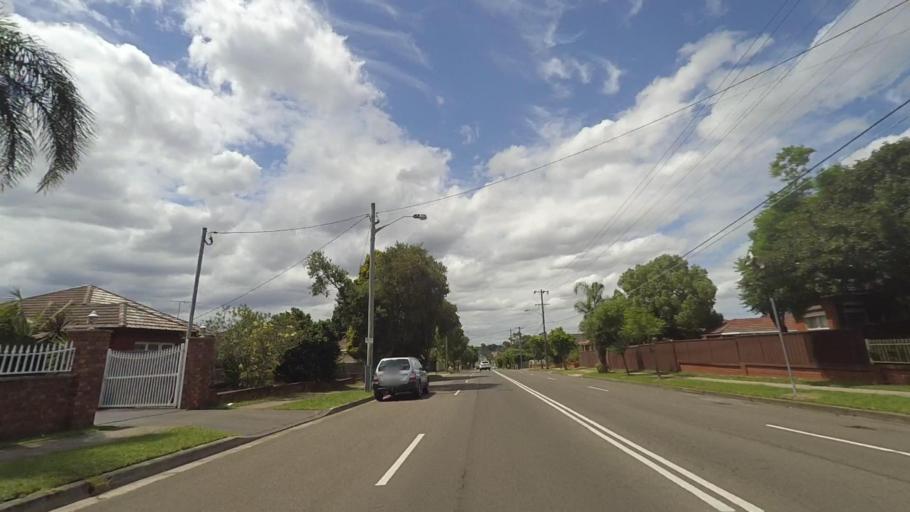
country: AU
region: New South Wales
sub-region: Fairfield
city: Fairfield Heights
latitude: -33.8752
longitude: 150.9440
